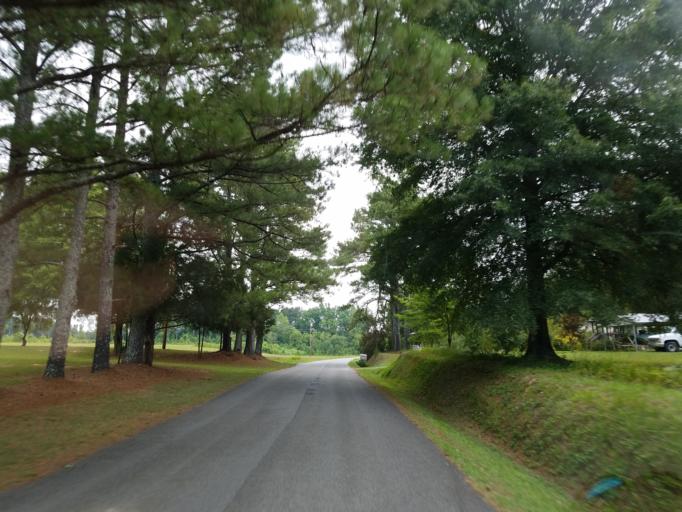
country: US
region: Georgia
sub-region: Bartow County
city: Rydal
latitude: 34.2669
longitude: -84.7592
